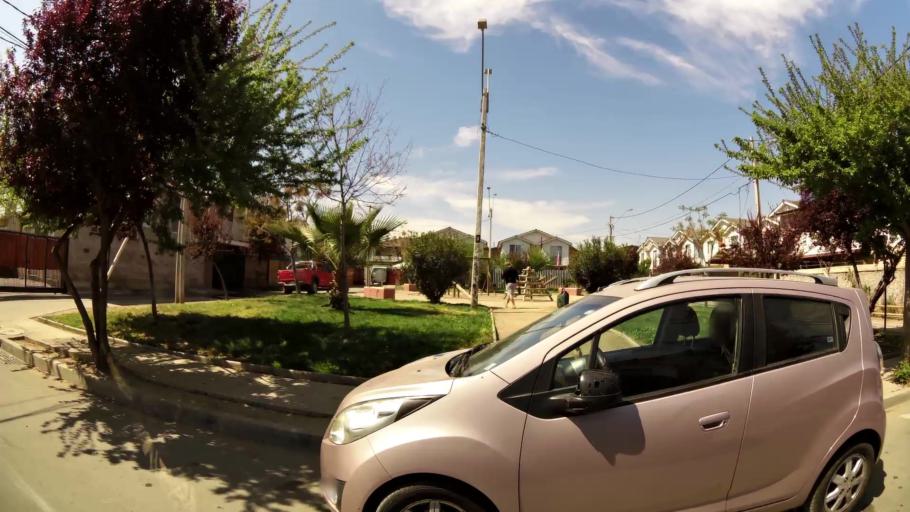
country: CL
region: Santiago Metropolitan
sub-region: Provincia de Santiago
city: Lo Prado
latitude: -33.3990
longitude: -70.7430
